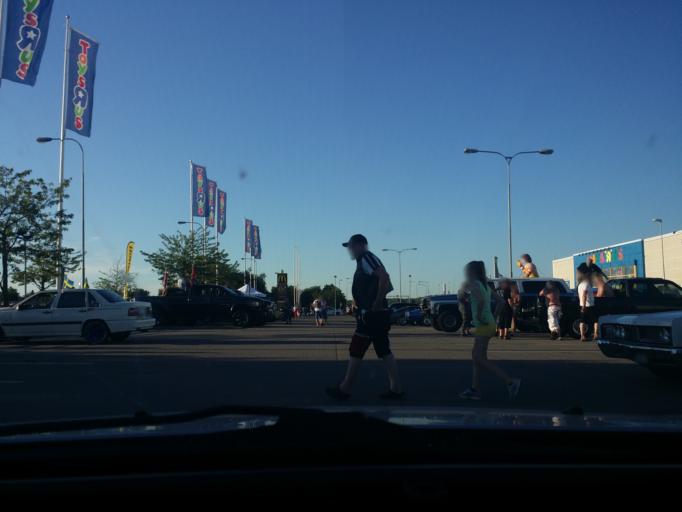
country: SE
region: Vaestmanland
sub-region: Vasteras
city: Hokasen
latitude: 59.6085
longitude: 16.6233
